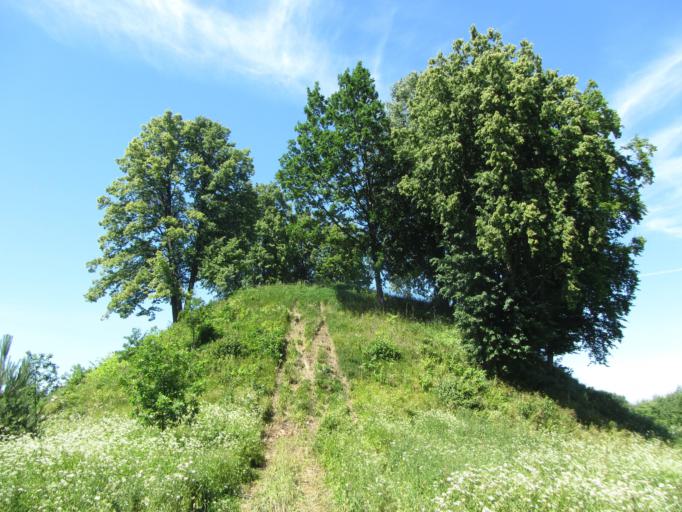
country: LT
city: Aukstadvaris
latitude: 54.6743
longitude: 24.4735
